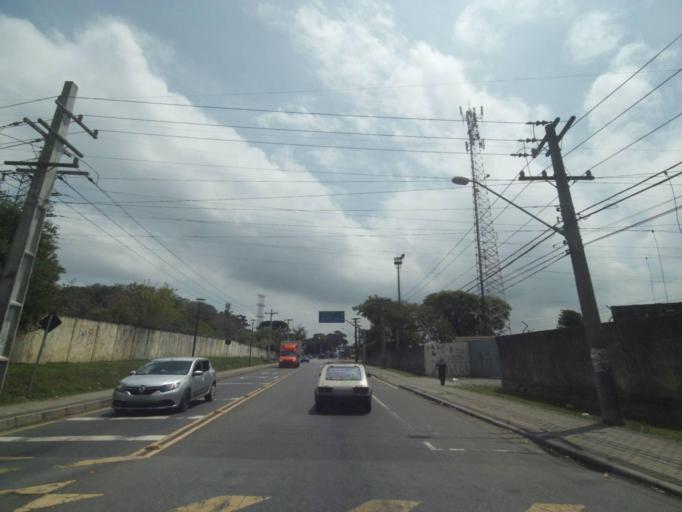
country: BR
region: Parana
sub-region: Curitiba
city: Curitiba
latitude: -25.4795
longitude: -49.3414
